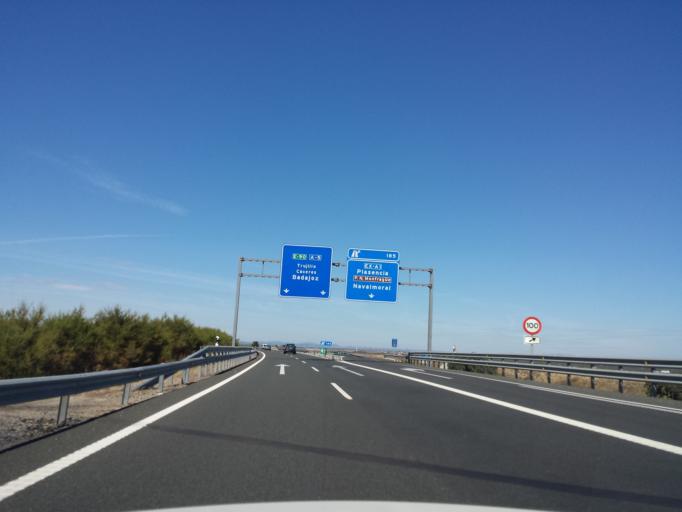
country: ES
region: Extremadura
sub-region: Provincia de Caceres
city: Millanes
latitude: 39.8717
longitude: -5.5828
